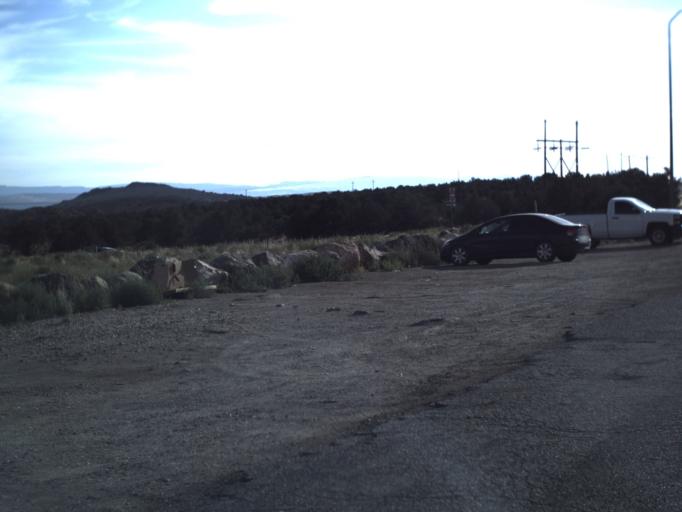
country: US
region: Utah
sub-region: Washington County
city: Toquerville
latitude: 37.2837
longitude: -113.3042
